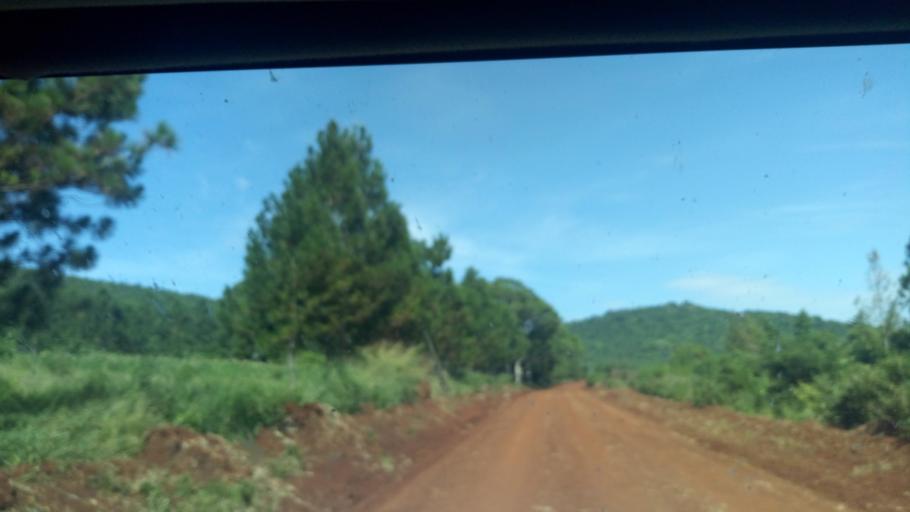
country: UG
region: Western Region
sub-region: Masindi District
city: Masindi
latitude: 1.6514
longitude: 31.7826
